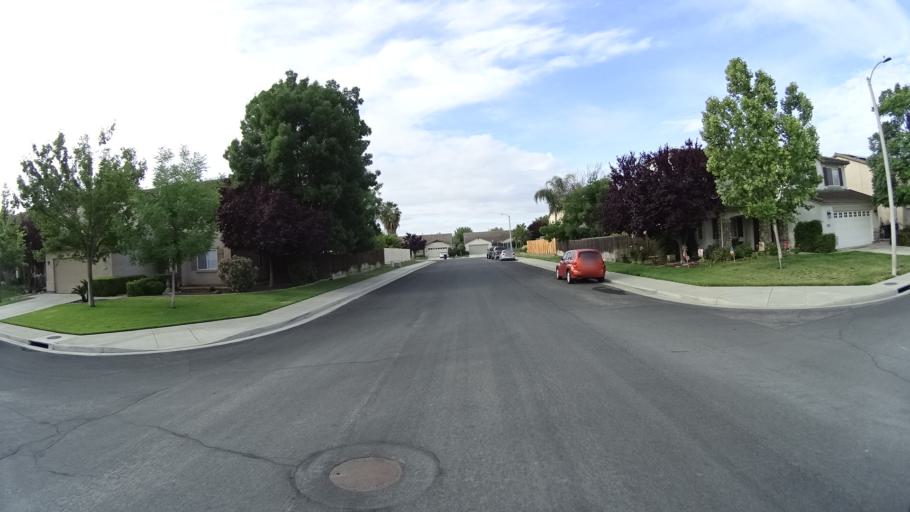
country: US
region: California
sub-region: Kings County
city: Hanford
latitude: 36.3447
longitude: -119.6802
